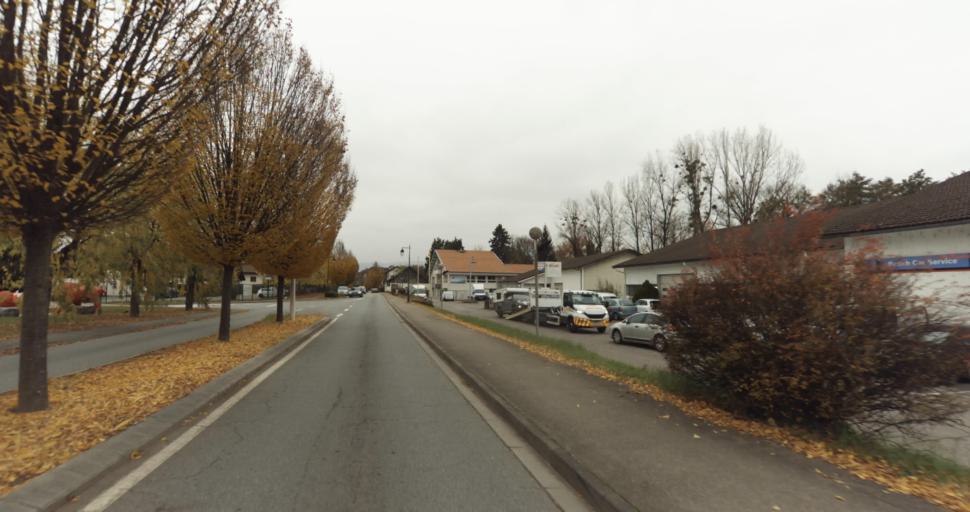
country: FR
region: Rhone-Alpes
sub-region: Departement de la Haute-Savoie
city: Epagny
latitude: 45.9291
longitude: 6.0833
